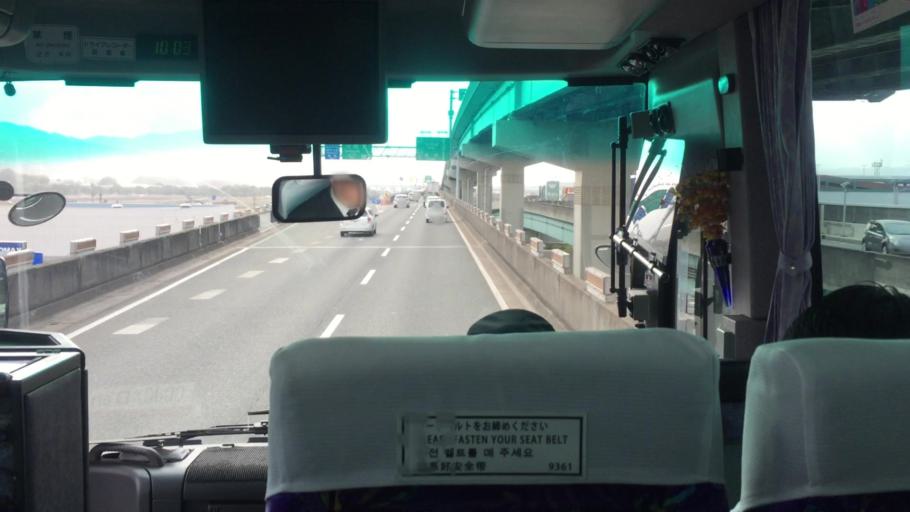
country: JP
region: Fukuoka
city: Onojo
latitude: 33.5743
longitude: 130.4526
